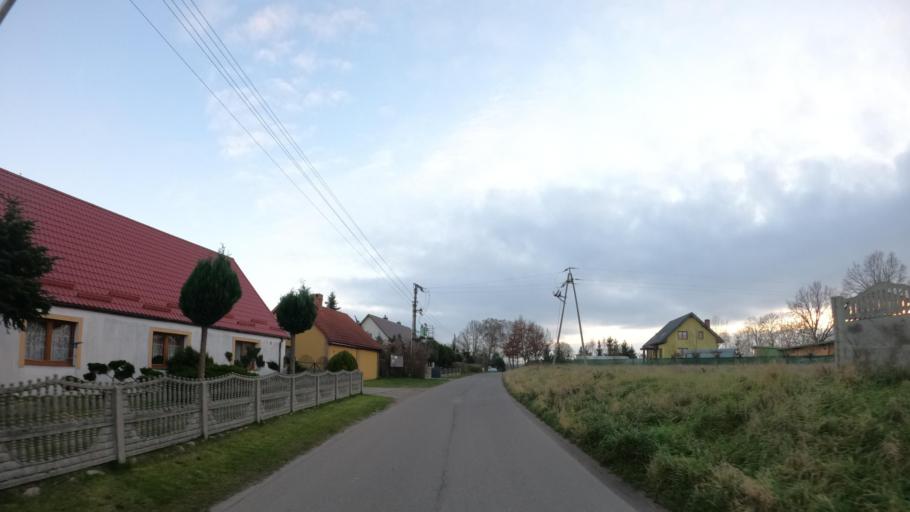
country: PL
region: West Pomeranian Voivodeship
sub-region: Powiat bialogardzki
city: Karlino
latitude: 54.0766
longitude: 15.8827
